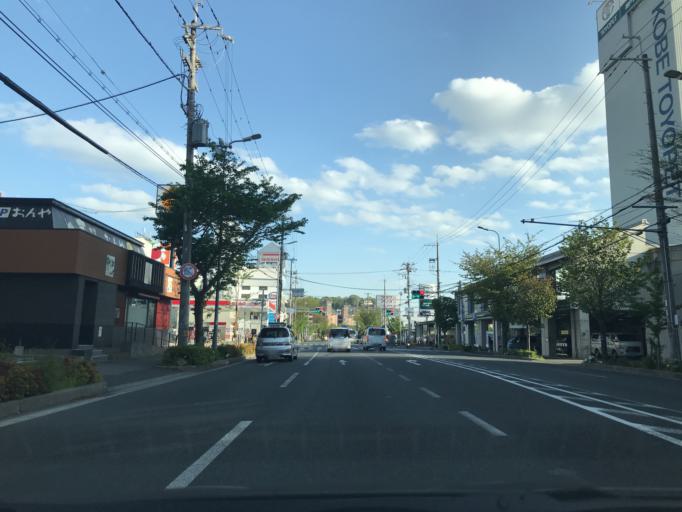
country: JP
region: Osaka
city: Ikeda
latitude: 34.8600
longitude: 135.4159
